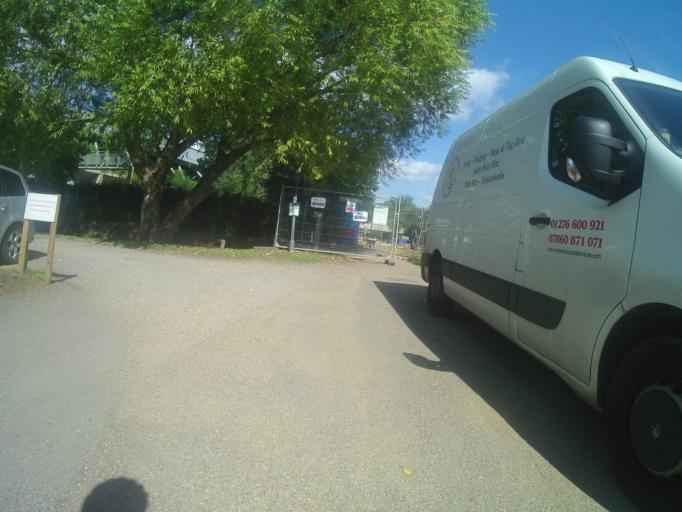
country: GB
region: England
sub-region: Surrey
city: Woking
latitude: 51.3207
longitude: -0.5616
